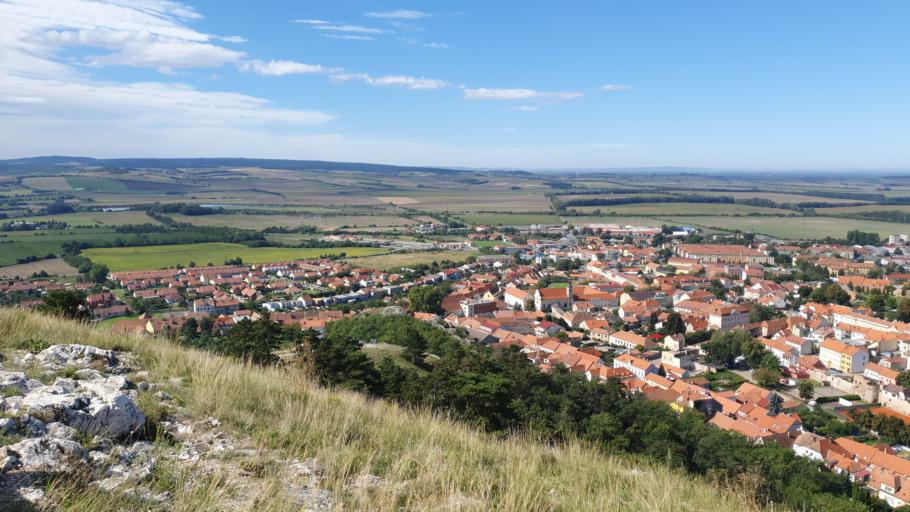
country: CZ
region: South Moravian
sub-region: Okres Breclav
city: Mikulov
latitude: 48.8065
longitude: 16.6452
